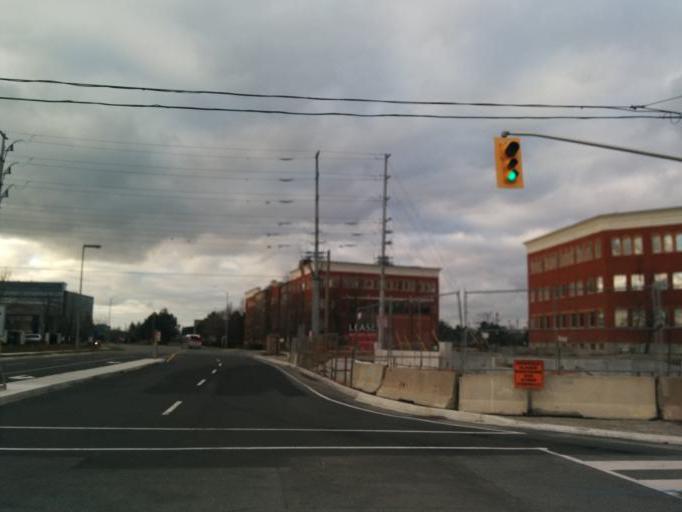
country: CA
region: Ontario
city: Etobicoke
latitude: 43.6557
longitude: -79.5981
